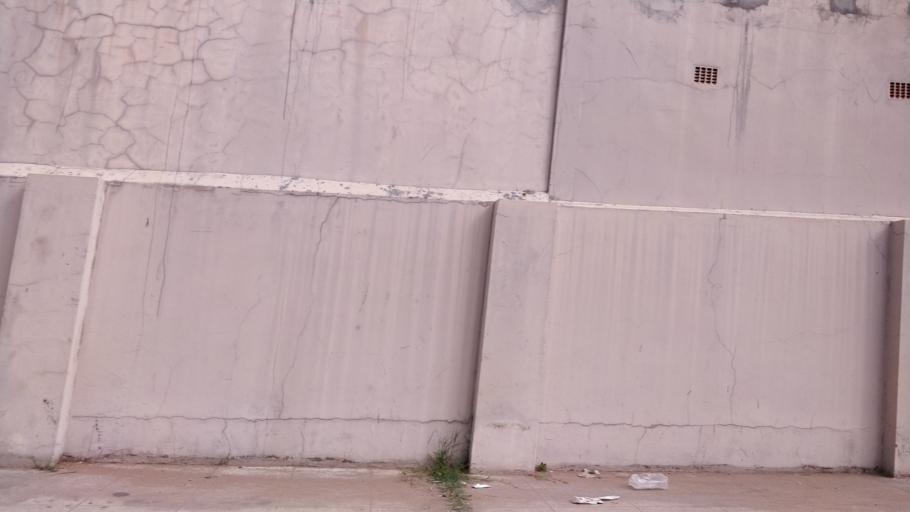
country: MZ
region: Maputo City
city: Maputo
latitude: -25.9764
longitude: 32.5750
